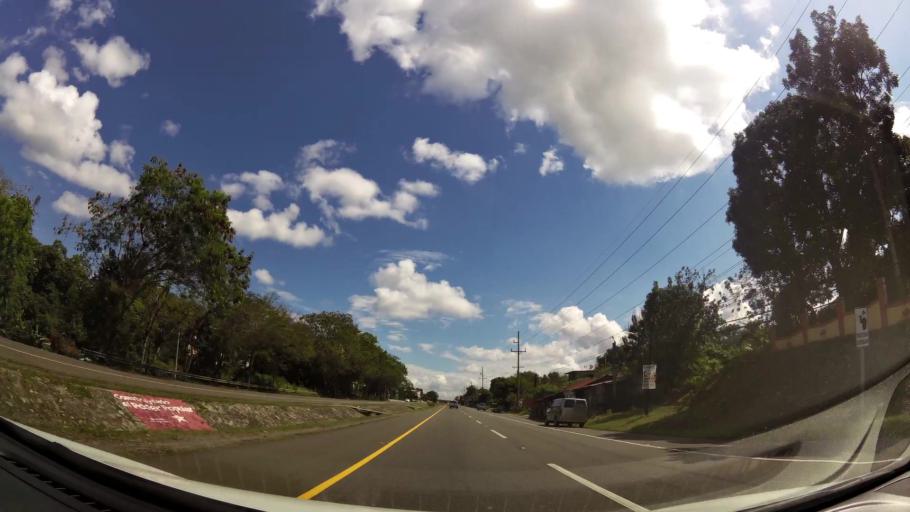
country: DO
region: La Vega
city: Rio Verde Arriba
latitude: 19.2908
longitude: -70.5759
